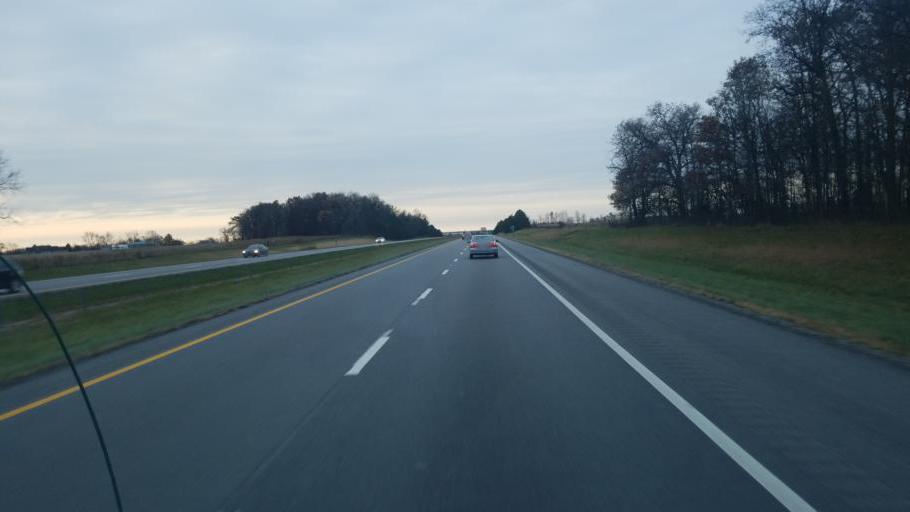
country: US
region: Ohio
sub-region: Auglaize County
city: Cridersville
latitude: 40.6131
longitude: -84.1495
